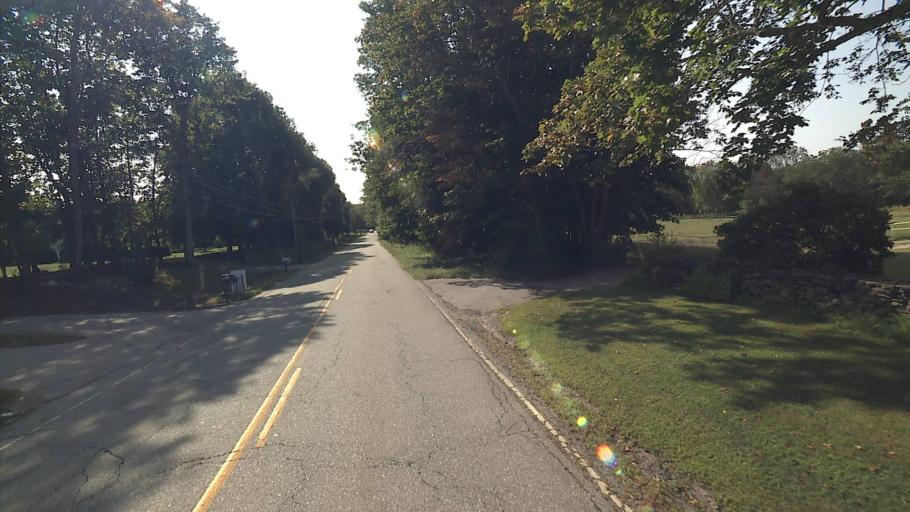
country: US
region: Connecticut
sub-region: Windham County
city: Willimantic
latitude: 41.6627
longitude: -72.2525
